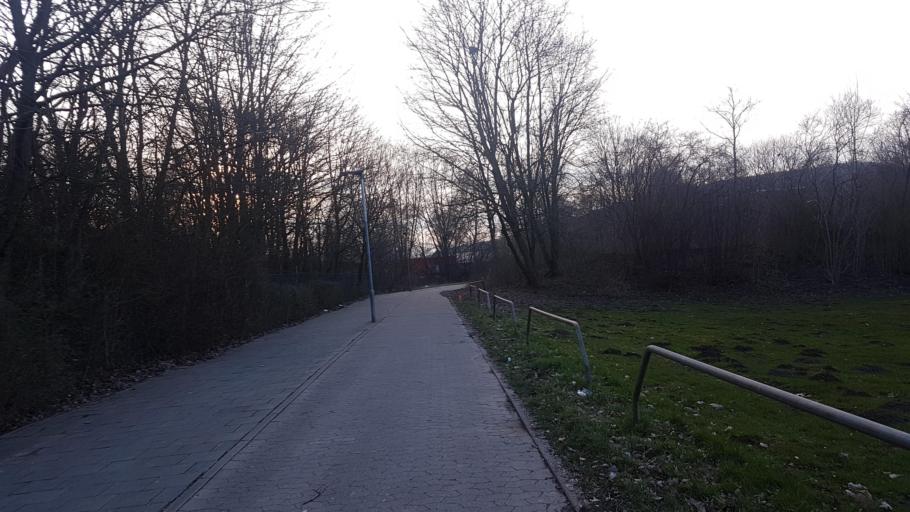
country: DE
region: Lower Saxony
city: Springe
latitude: 52.2014
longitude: 9.5618
